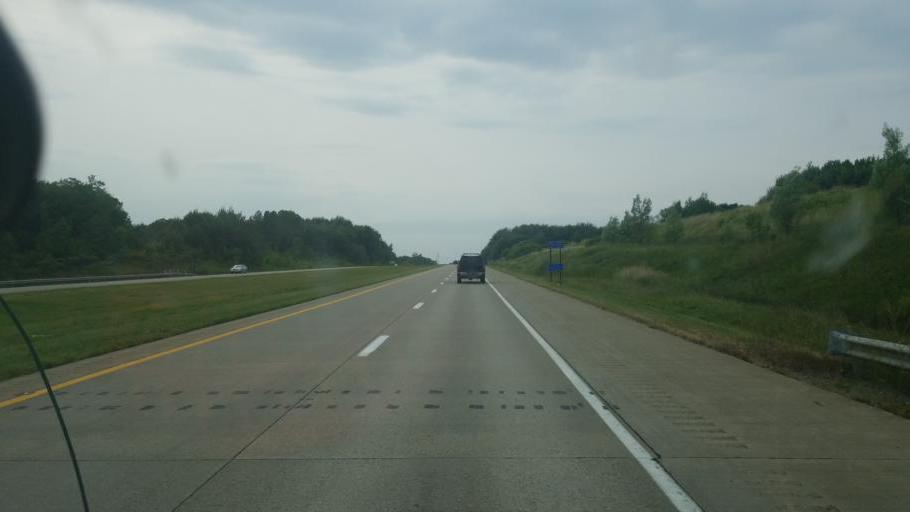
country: US
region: Pennsylvania
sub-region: Erie County
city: North East
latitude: 42.1479
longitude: -79.8487
